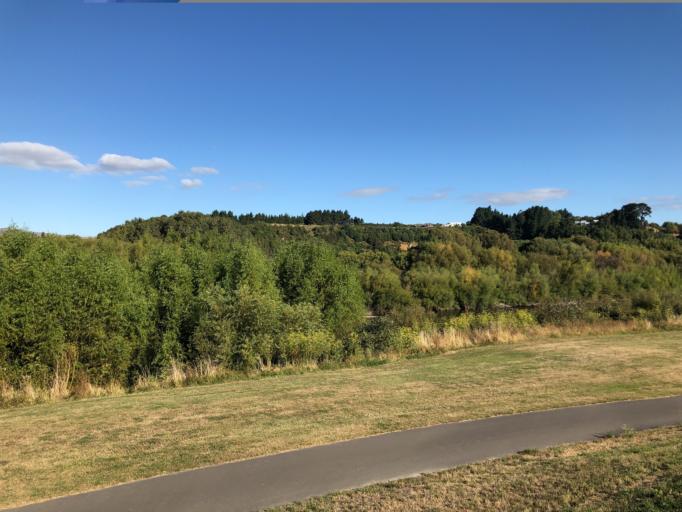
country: NZ
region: Manawatu-Wanganui
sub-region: Palmerston North City
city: Palmerston North
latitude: -40.3728
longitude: 175.6415
